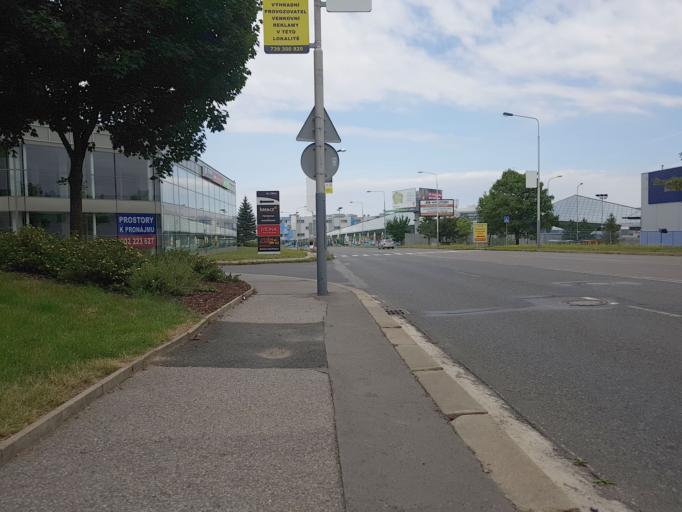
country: CZ
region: Central Bohemia
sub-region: Okres Praha-Zapad
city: Pruhonice
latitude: 50.0056
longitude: 14.5728
